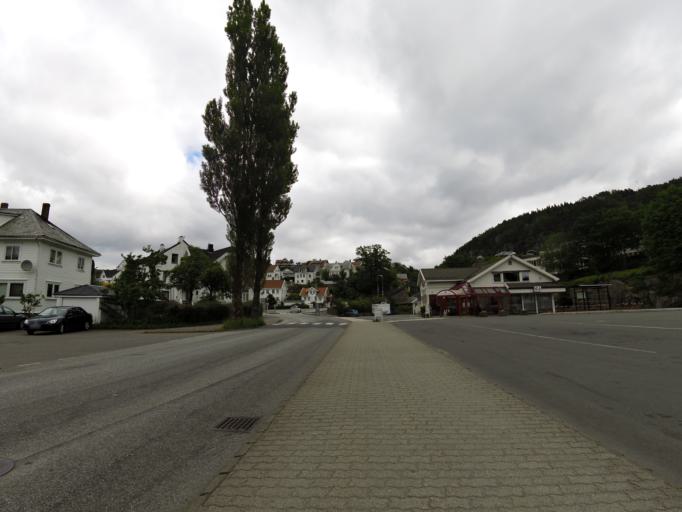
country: NO
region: Vest-Agder
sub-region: Flekkefjord
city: Flekkefjord
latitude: 58.2948
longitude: 6.6666
